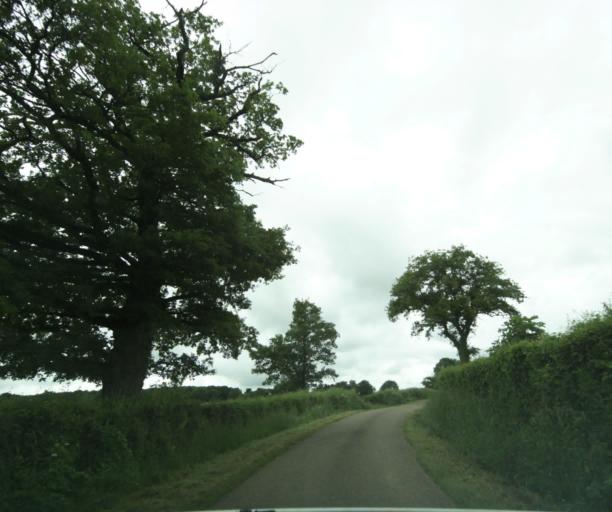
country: FR
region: Bourgogne
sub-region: Departement de Saone-et-Loire
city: Charolles
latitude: 46.4620
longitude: 4.2873
